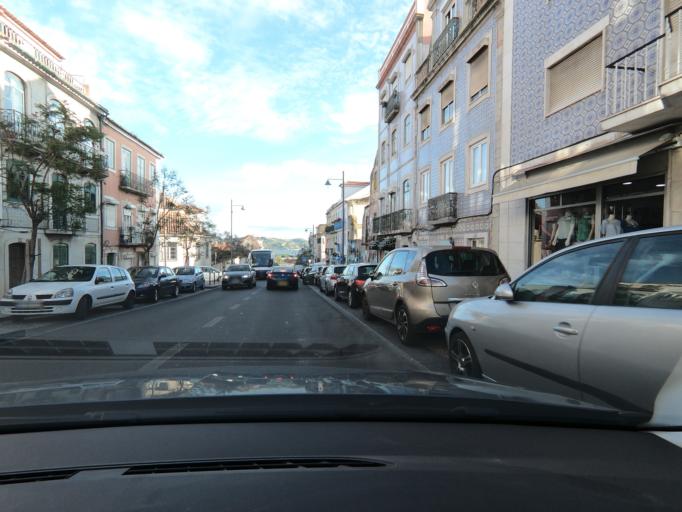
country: PT
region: Lisbon
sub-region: Oeiras
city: Alges
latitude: 38.7036
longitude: -9.1995
